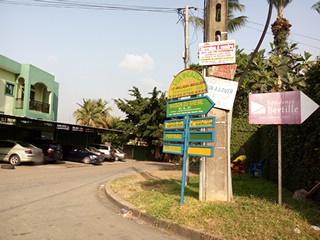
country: CI
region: Lagunes
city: Abidjan
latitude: 5.3578
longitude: -3.9914
